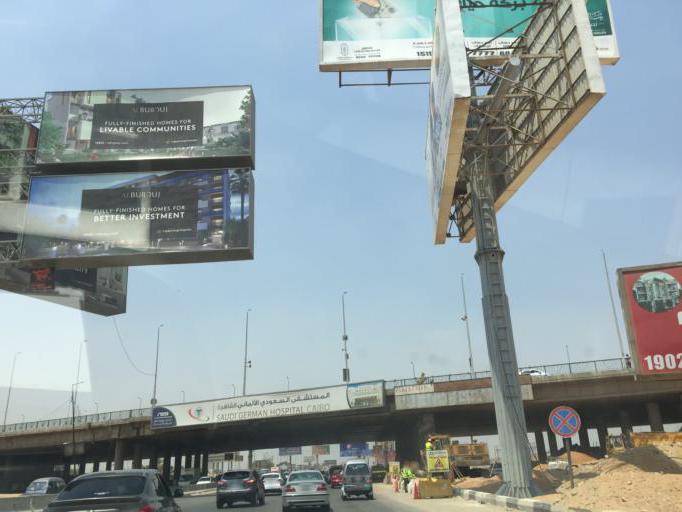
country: EG
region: Muhafazat al Qalyubiyah
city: Al Khankah
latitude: 30.0798
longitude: 31.4365
